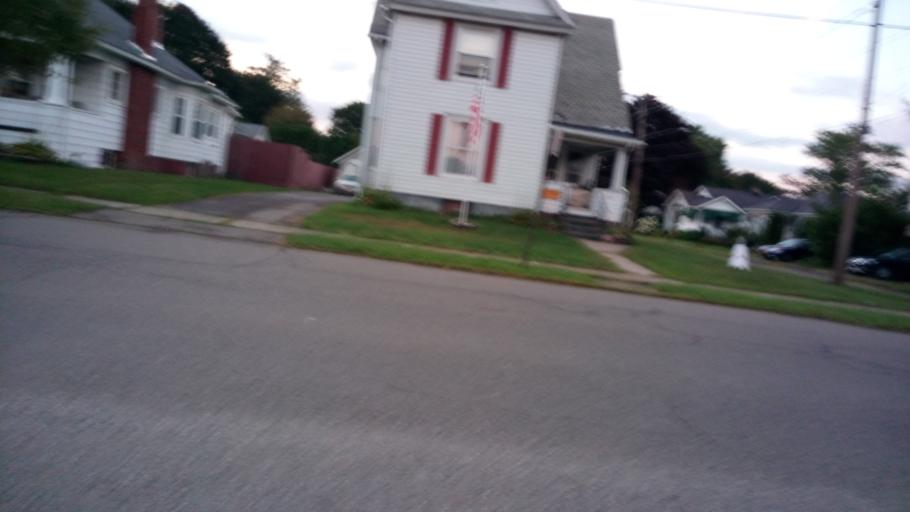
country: US
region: New York
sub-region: Chemung County
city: Elmira
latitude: 42.1030
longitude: -76.8235
